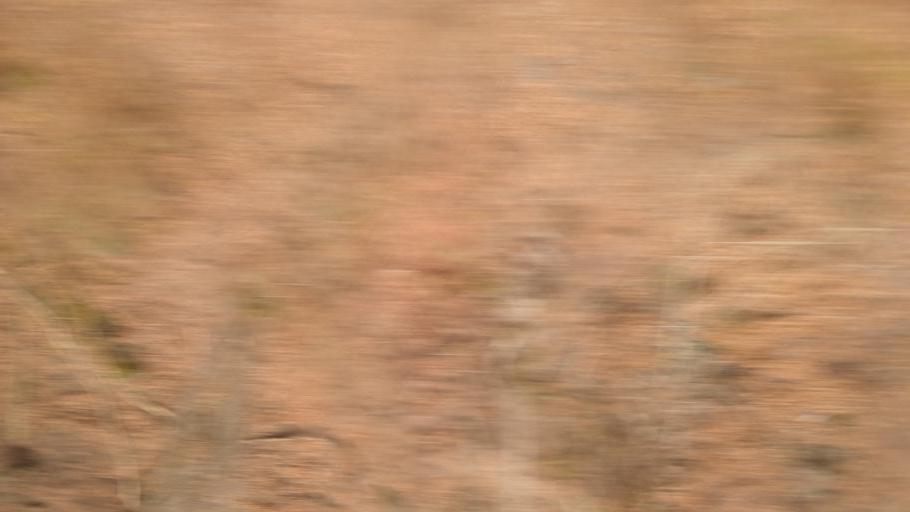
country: JP
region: Nagano
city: Tatsuno
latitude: 35.9887
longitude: 137.8463
